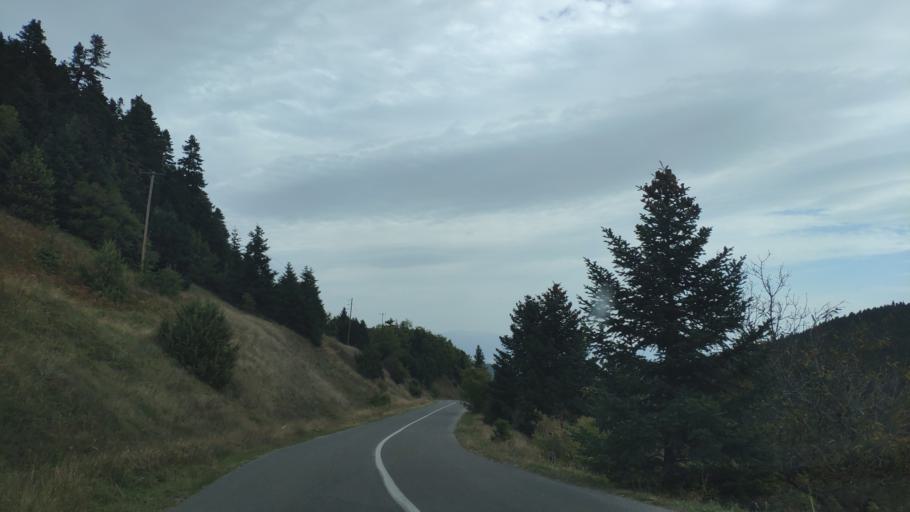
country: GR
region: Central Greece
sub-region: Nomos Fthiotidos
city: Stavros
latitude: 38.7251
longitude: 22.3345
